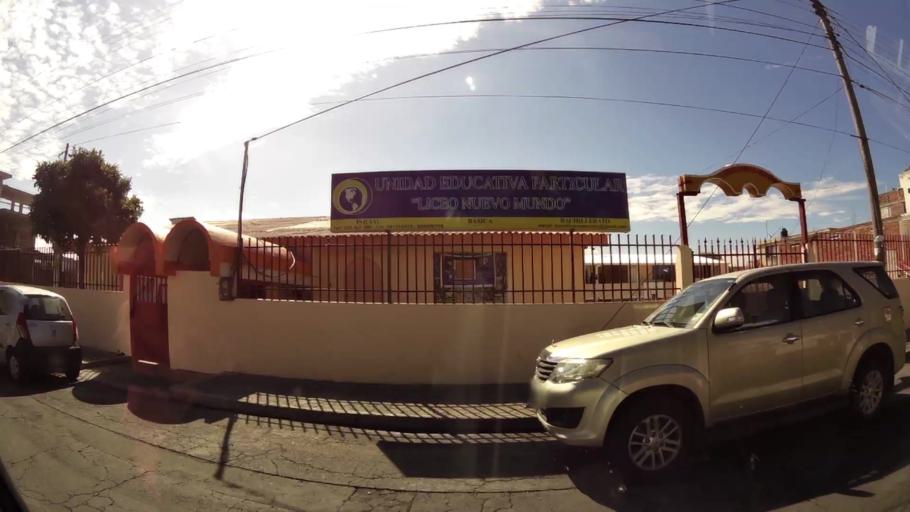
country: EC
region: Chimborazo
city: Riobamba
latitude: -1.6568
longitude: -78.6658
